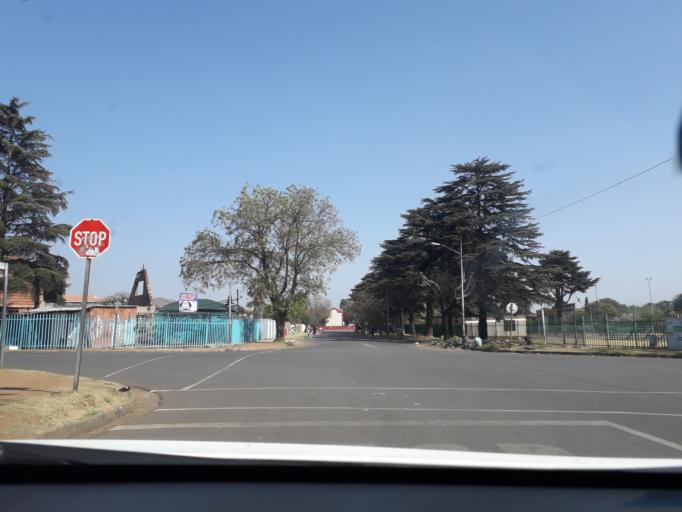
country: ZA
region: Gauteng
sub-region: City of Johannesburg Metropolitan Municipality
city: Modderfontein
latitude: -26.1017
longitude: 28.2392
